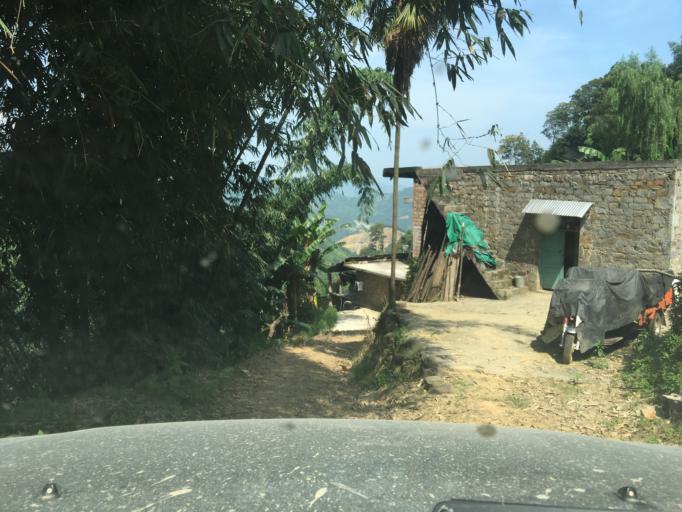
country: CN
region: Guangxi Zhuangzu Zizhiqu
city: Xinzhou
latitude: 25.0416
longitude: 105.8693
